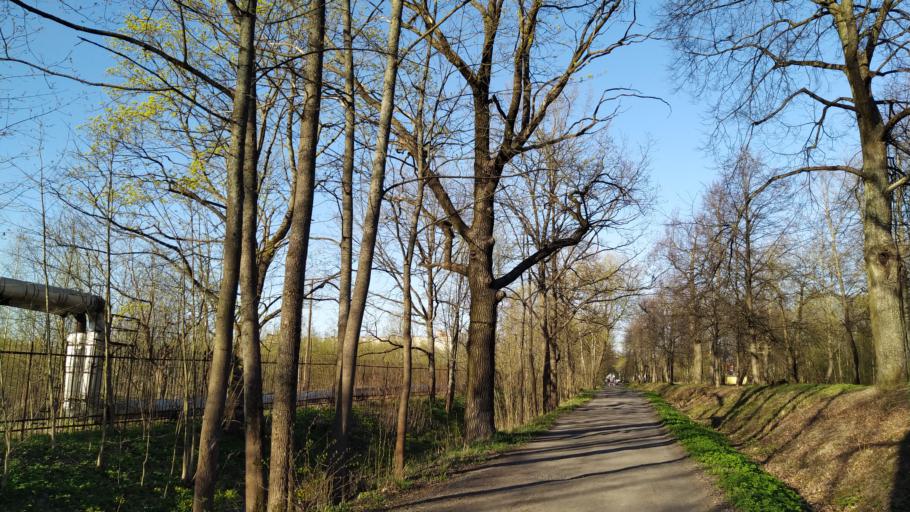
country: RU
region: St.-Petersburg
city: Pushkin
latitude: 59.7074
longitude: 30.3727
